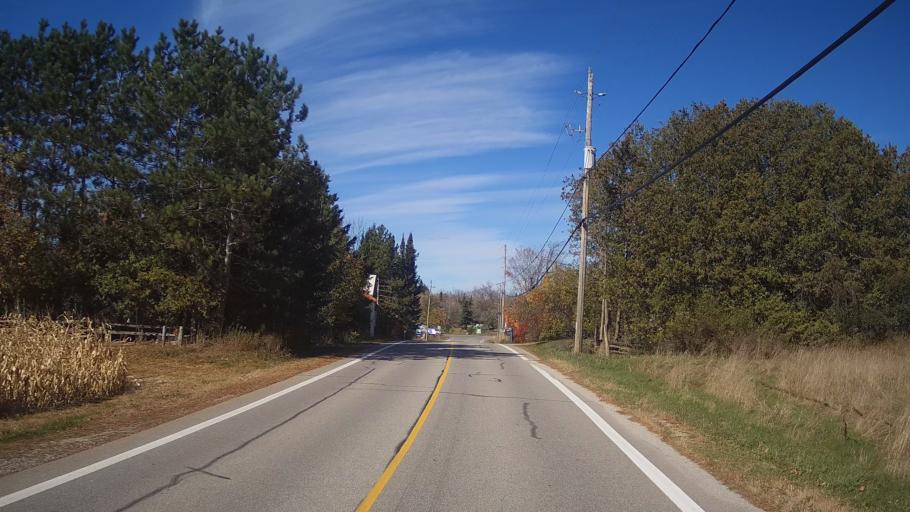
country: CA
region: Ontario
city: Perth
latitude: 44.8816
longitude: -76.3064
